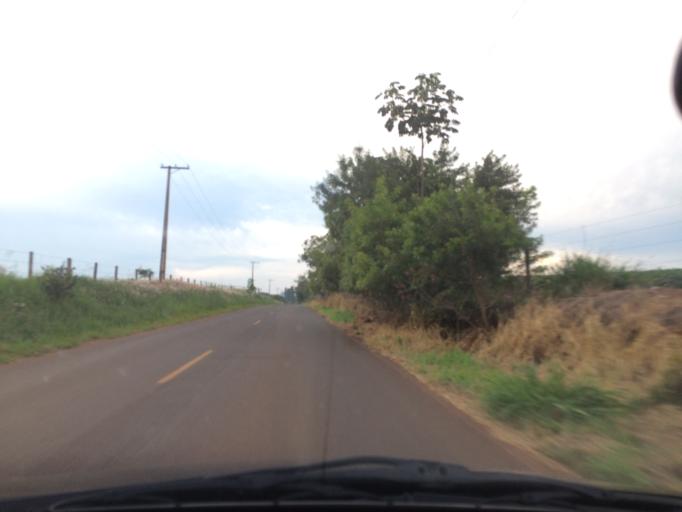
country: BR
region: Sao Paulo
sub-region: Casa Branca
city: Casa Branca
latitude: -21.7569
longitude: -47.1192
